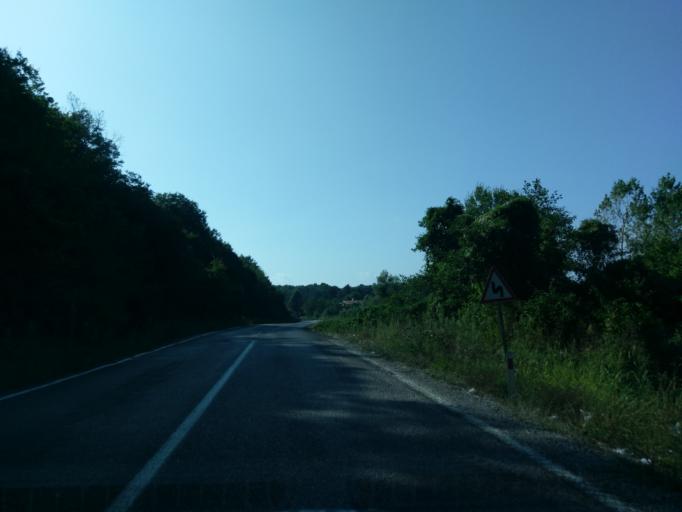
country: TR
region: Sinop
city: Yenikonak
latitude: 41.9458
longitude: 34.7486
